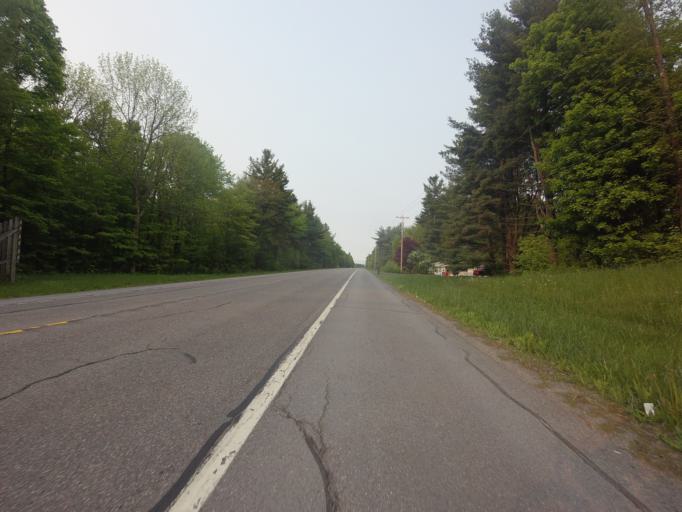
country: US
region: New York
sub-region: St. Lawrence County
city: Gouverneur
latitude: 44.1141
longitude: -75.3963
